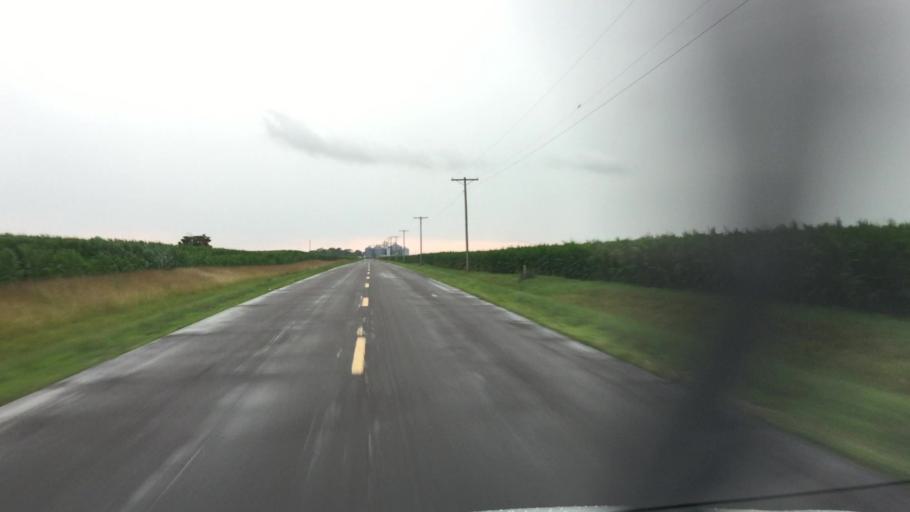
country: US
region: Illinois
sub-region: Hancock County
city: Carthage
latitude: 40.5201
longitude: -91.1436
